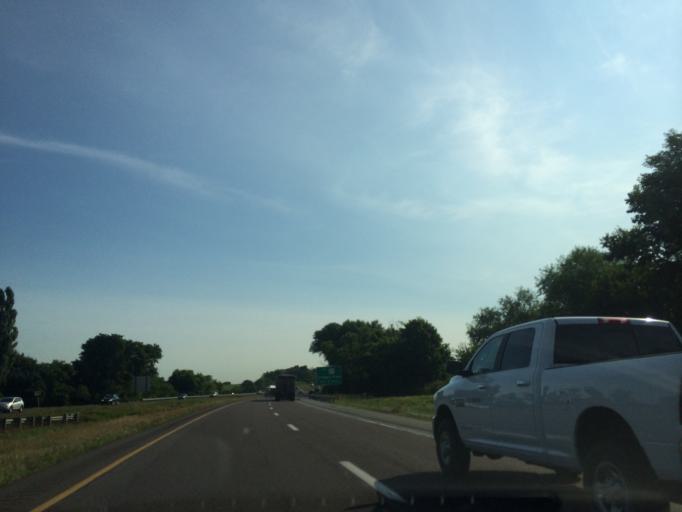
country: US
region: Pennsylvania
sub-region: Lancaster County
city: Lancaster
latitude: 40.0759
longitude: -76.2848
